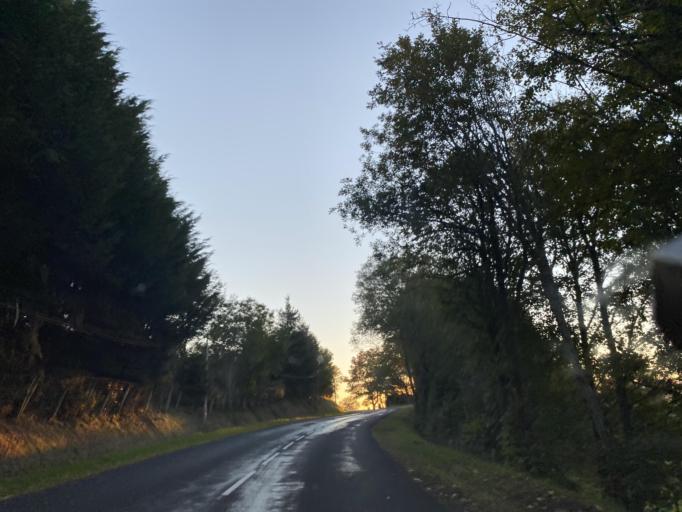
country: FR
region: Rhone-Alpes
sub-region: Departement de la Loire
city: Noiretable
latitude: 45.7915
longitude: 3.6960
